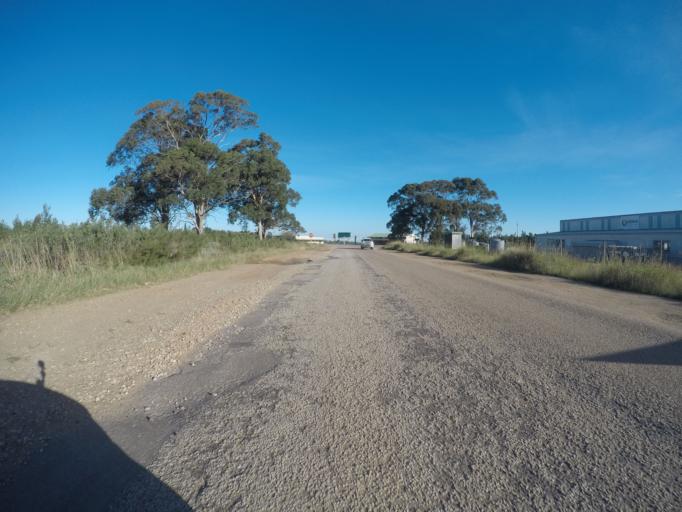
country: ZA
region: Eastern Cape
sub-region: Cacadu District Municipality
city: Kareedouw
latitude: -34.0043
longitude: 24.2342
